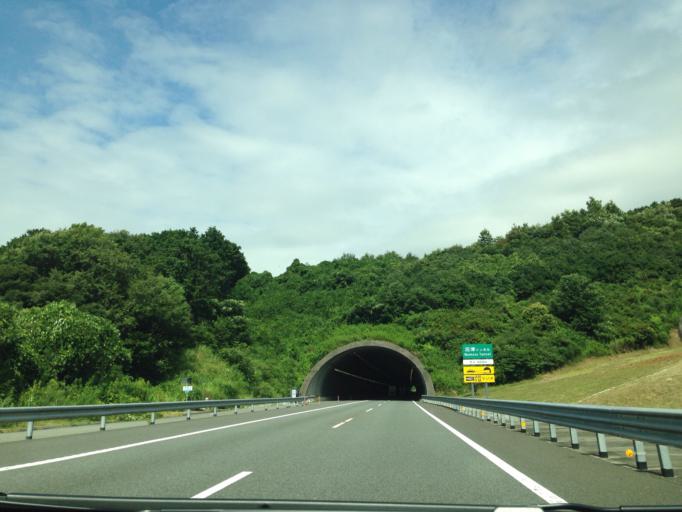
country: JP
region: Shizuoka
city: Numazu
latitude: 35.1548
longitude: 138.7947
